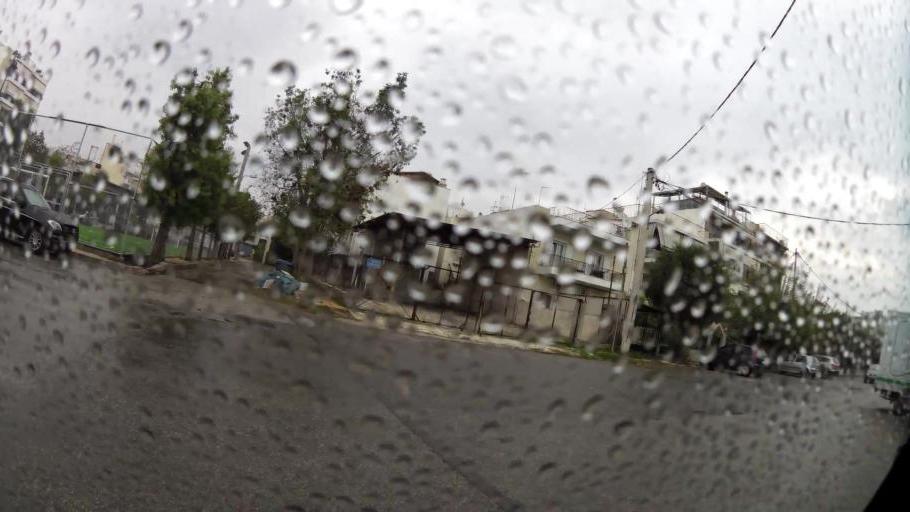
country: GR
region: Attica
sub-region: Nomarchia Athinas
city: Agioi Anargyroi
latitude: 38.0179
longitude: 23.7198
